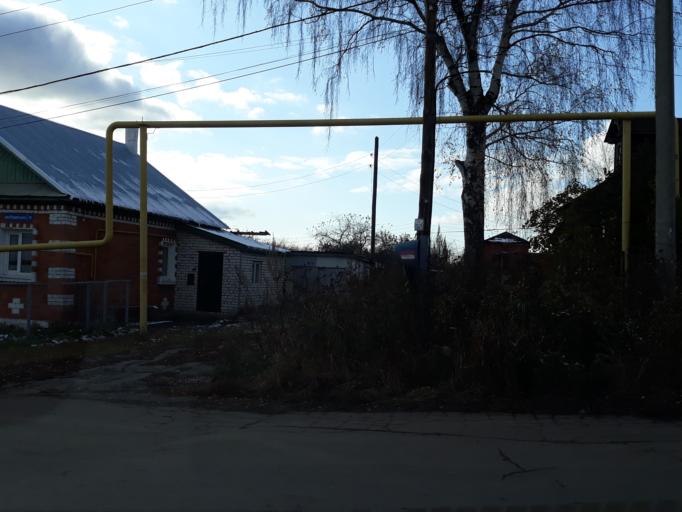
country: RU
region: Nizjnij Novgorod
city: Afonino
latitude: 56.2320
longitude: 44.0152
